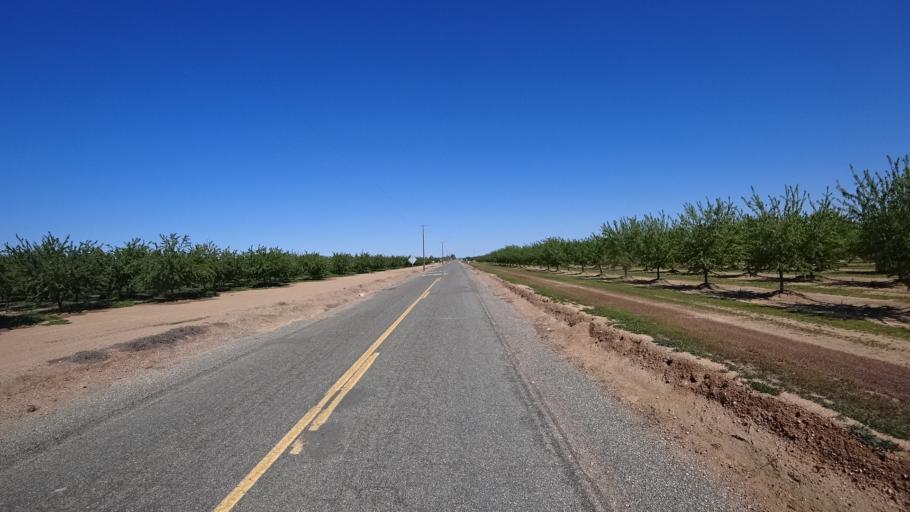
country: US
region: California
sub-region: Glenn County
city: Orland
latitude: 39.6693
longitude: -122.2530
